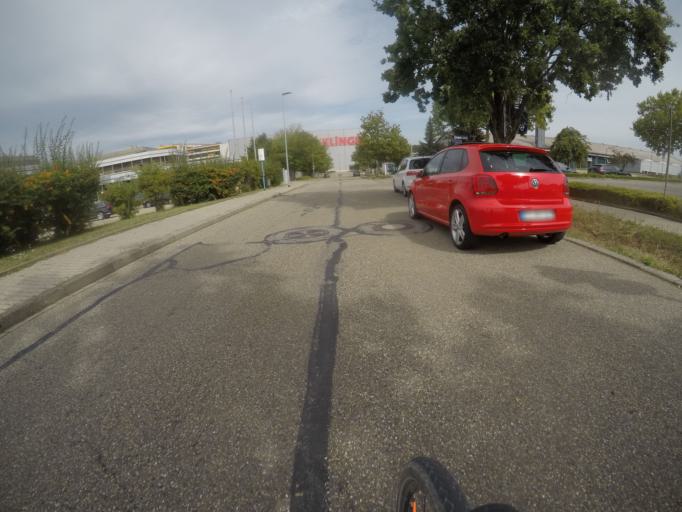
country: DE
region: Baden-Wuerttemberg
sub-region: Karlsruhe Region
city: Eutingen
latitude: 48.8864
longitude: 8.7538
